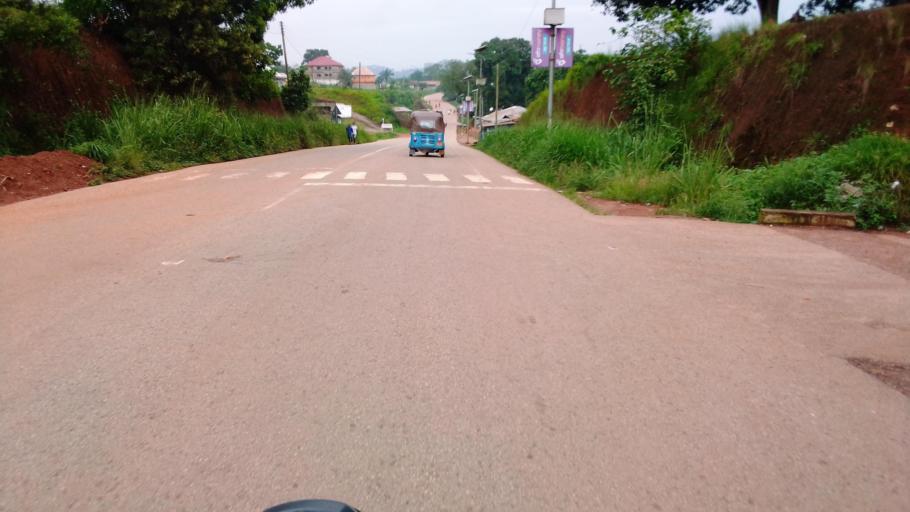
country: SL
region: Eastern Province
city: Kenema
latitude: 7.8760
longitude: -11.1773
